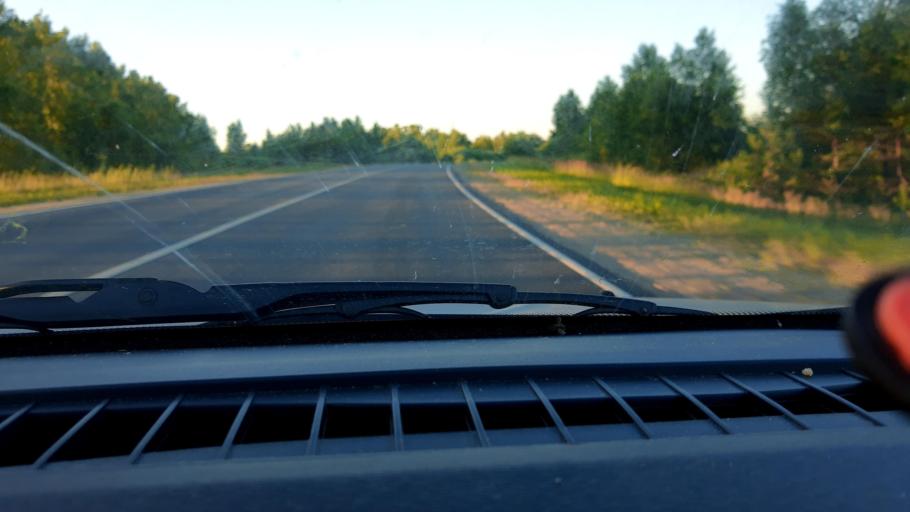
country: RU
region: Nizjnij Novgorod
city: Vladimirskoye
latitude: 56.9563
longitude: 45.0947
